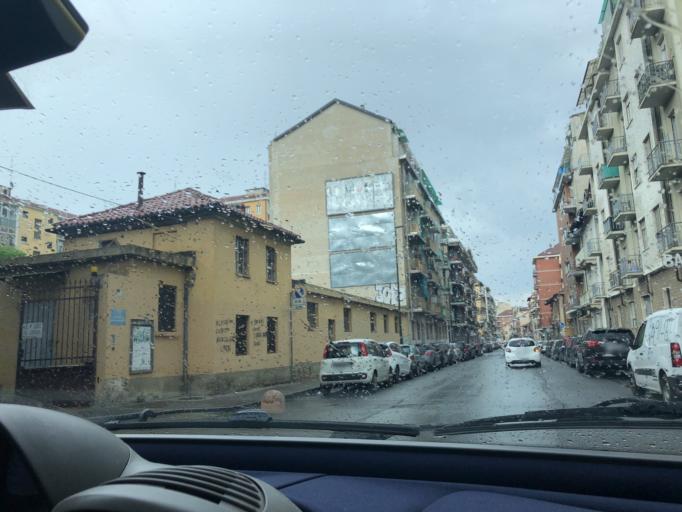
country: IT
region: Piedmont
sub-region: Provincia di Torino
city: Lesna
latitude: 45.0794
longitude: 7.6284
